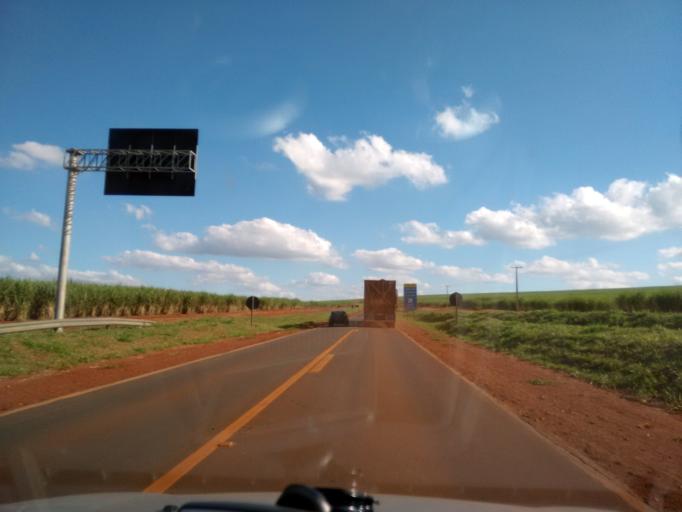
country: BR
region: Sao Paulo
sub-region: Americo Brasiliense
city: Americo Brasiliense
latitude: -21.6161
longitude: -48.0335
